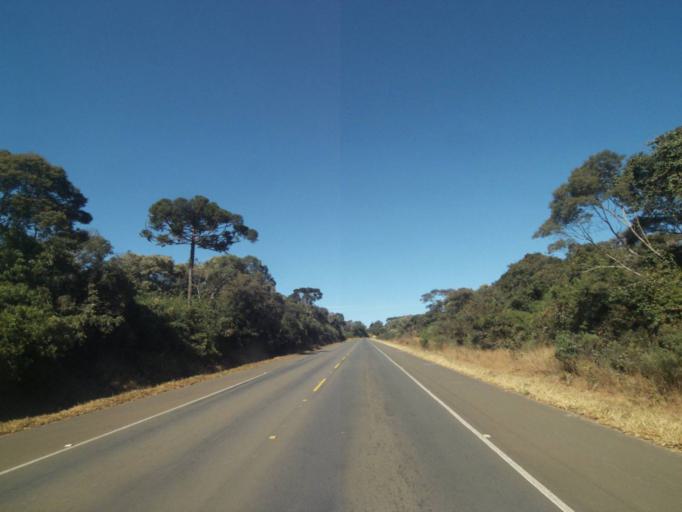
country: BR
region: Parana
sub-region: Tibagi
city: Tibagi
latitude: -24.6599
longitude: -50.4522
